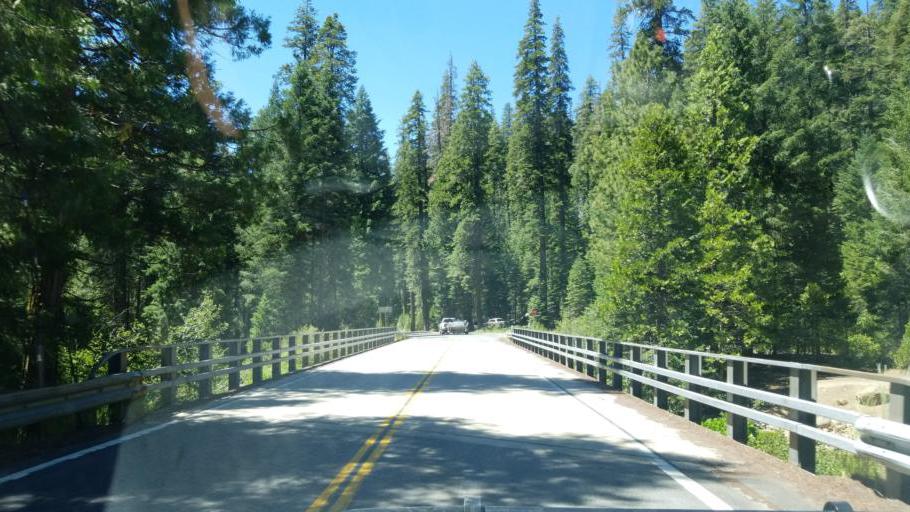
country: US
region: California
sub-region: Plumas County
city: Chester
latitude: 40.2462
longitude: -121.4482
